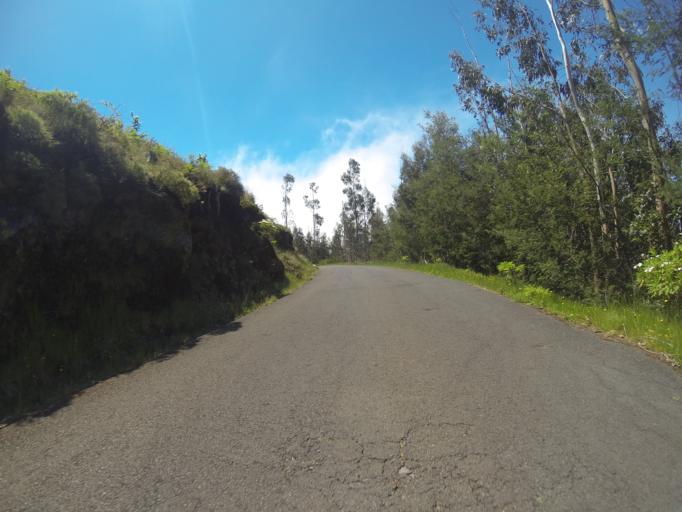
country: PT
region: Madeira
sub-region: Funchal
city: Nossa Senhora do Monte
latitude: 32.7006
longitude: -16.9074
